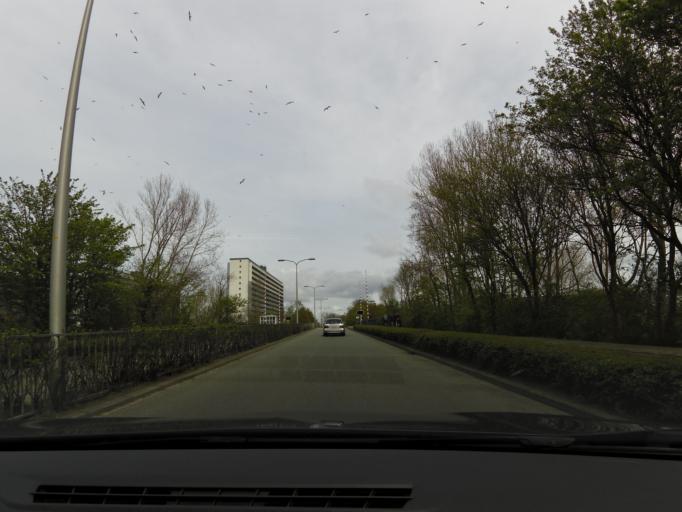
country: NL
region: South Holland
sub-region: Gemeente Katwijk
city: Katwijk aan den Rijn
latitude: 52.2029
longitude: 4.4181
